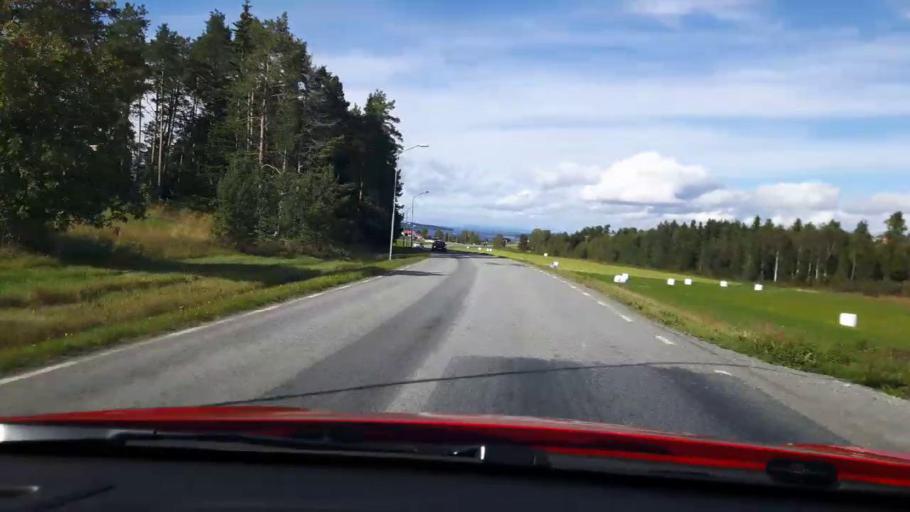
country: SE
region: Jaemtland
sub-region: OEstersunds Kommun
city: Ostersund
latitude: 63.0964
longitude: 14.4384
